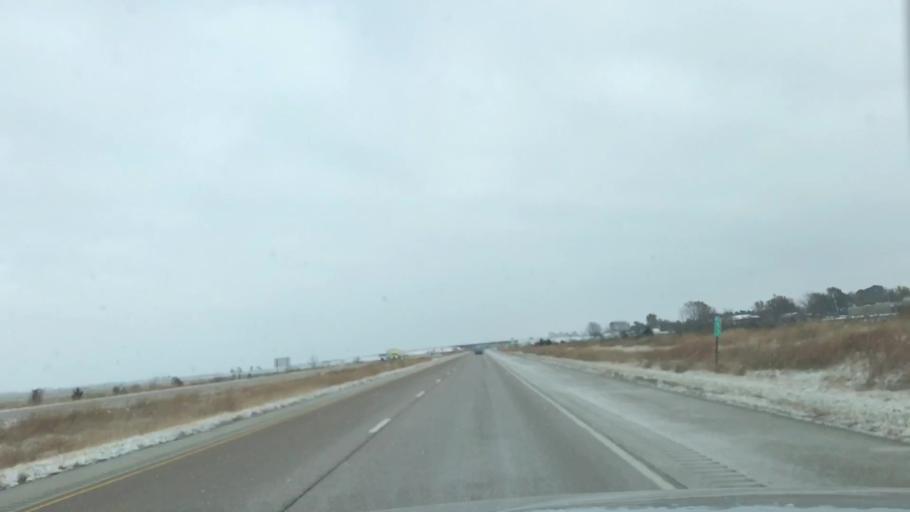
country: US
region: Illinois
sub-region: Montgomery County
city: Litchfield
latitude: 39.1813
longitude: -89.6770
